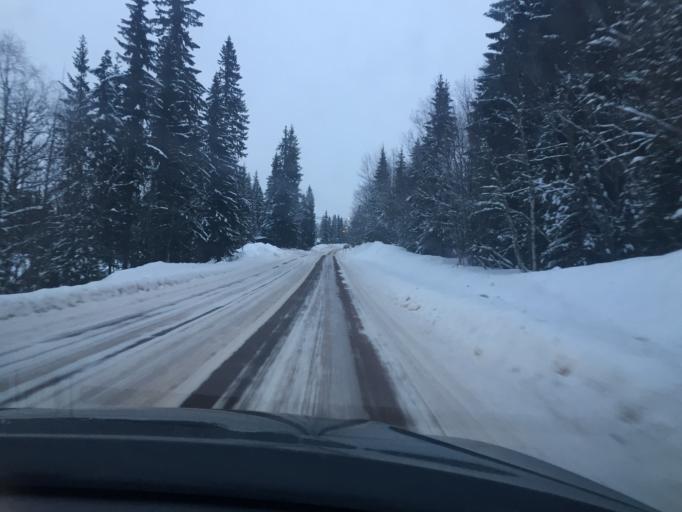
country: SE
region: Dalarna
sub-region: Malung-Saelens kommun
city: Malung
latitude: 61.1677
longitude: 13.1643
